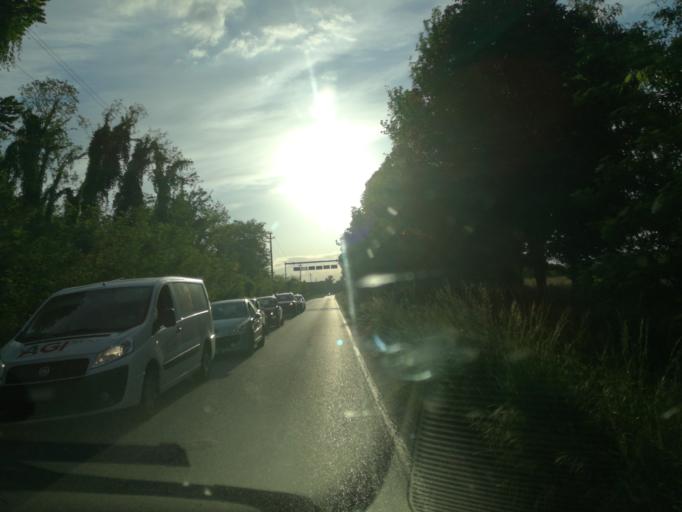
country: IT
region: Lombardy
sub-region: Provincia di Lecco
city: Merate
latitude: 45.6751
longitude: 9.4202
